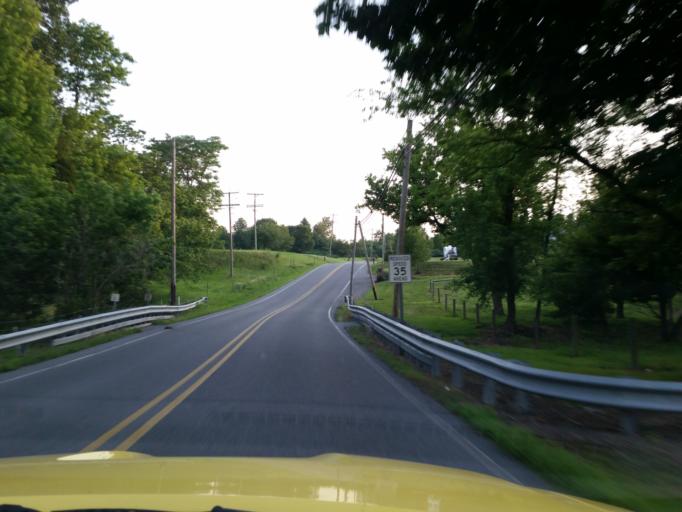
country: US
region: Pennsylvania
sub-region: Lebanon County
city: Jonestown
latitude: 40.4164
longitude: -76.4638
